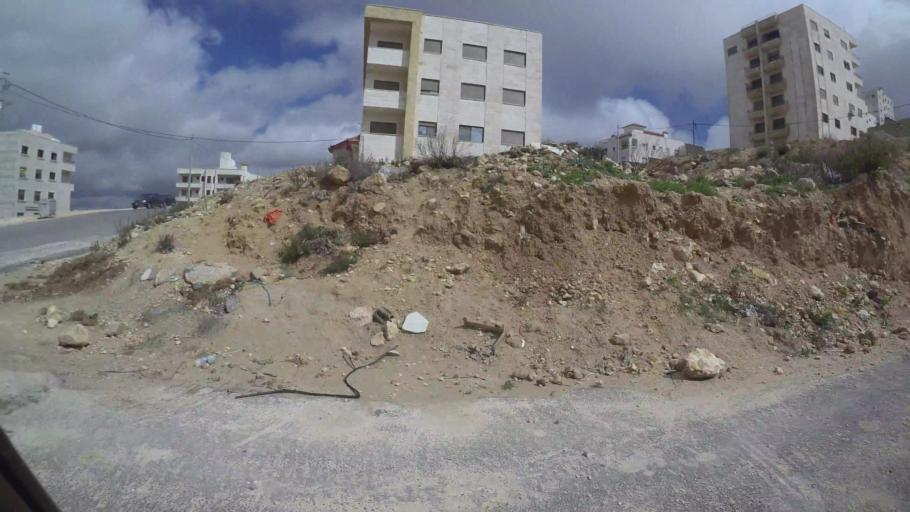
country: JO
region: Amman
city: Al Jubayhah
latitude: 32.0668
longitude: 35.8757
